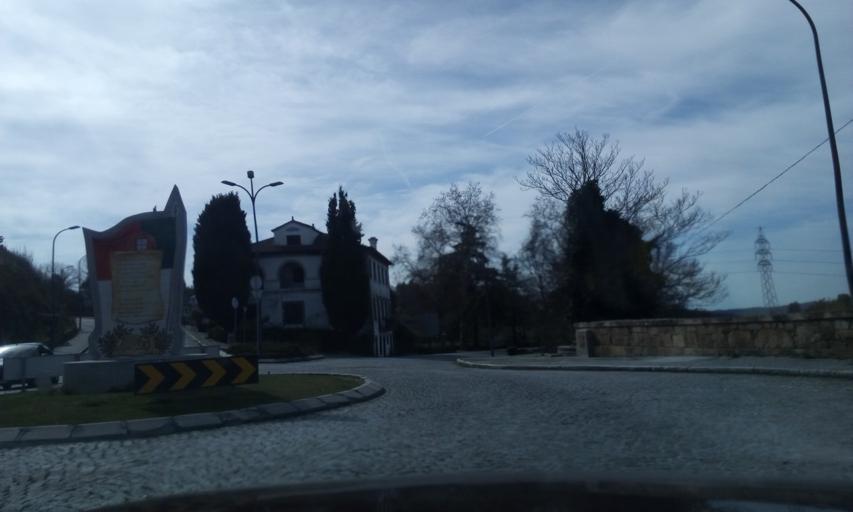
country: PT
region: Guarda
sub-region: Celorico da Beira
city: Celorico da Beira
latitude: 40.6331
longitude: -7.3967
